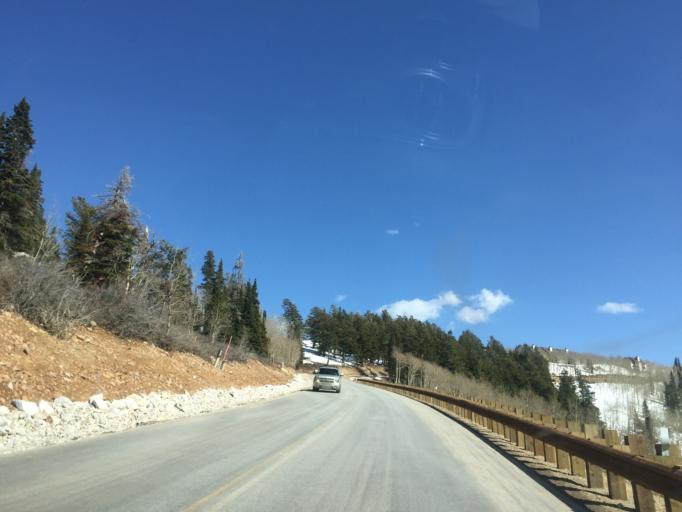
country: US
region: Utah
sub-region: Weber County
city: Wolf Creek
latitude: 41.3737
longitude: -111.7728
